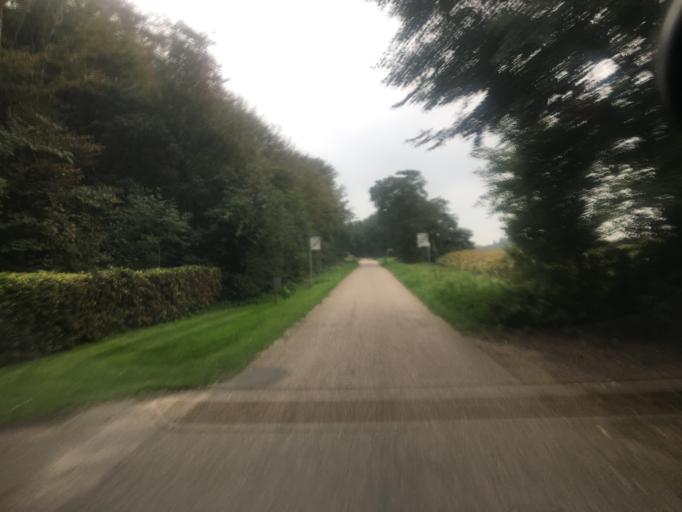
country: DE
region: Schleswig-Holstein
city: Ellhoft
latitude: 54.9456
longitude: 8.9640
